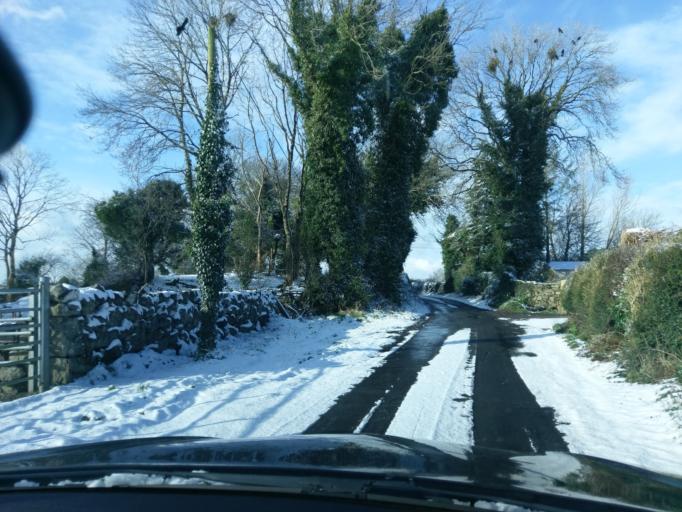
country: IE
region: Connaught
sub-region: County Galway
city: Athenry
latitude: 53.2065
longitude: -8.8130
